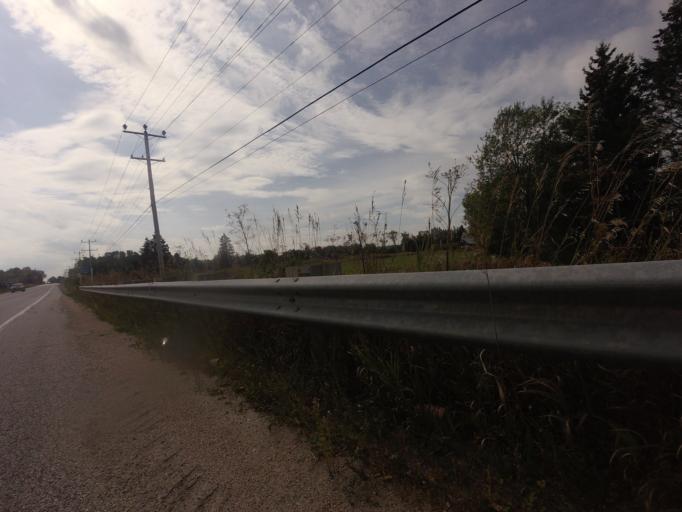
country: CA
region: Quebec
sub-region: Outaouais
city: Wakefield
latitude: 45.8740
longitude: -76.0248
